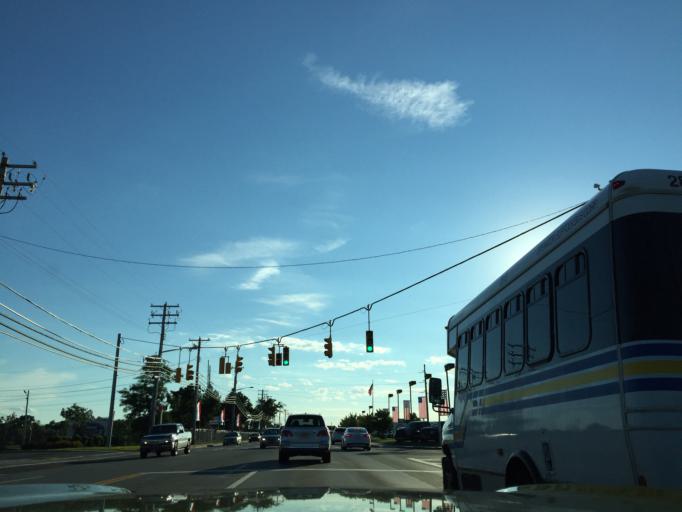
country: US
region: New York
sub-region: Suffolk County
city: Riverhead
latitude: 40.9244
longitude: -72.7031
